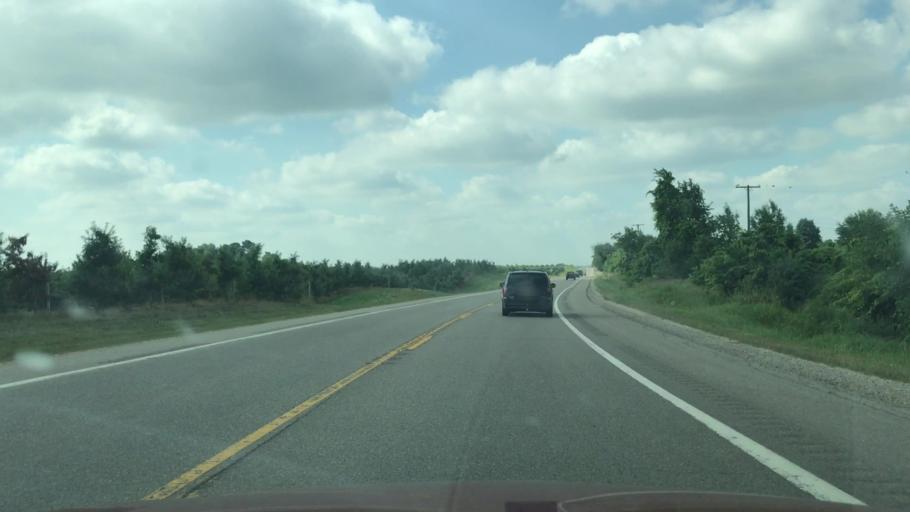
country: US
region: Michigan
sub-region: Kent County
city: Kent City
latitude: 43.2486
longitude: -85.8105
